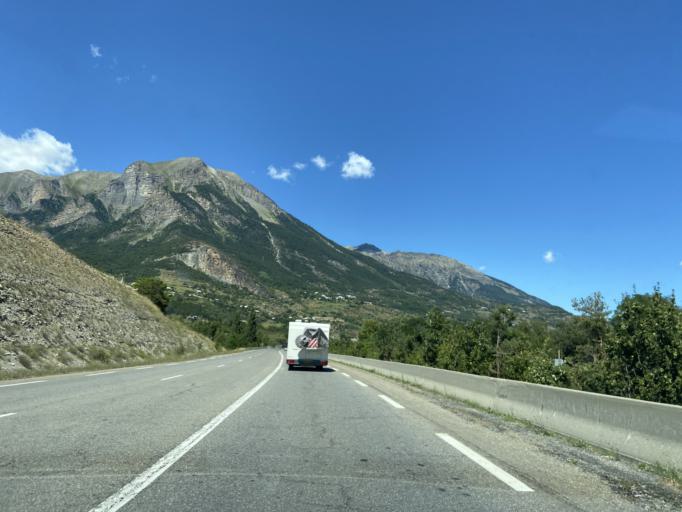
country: FR
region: Provence-Alpes-Cote d'Azur
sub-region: Departement des Hautes-Alpes
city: Embrun
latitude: 44.6067
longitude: 6.5292
